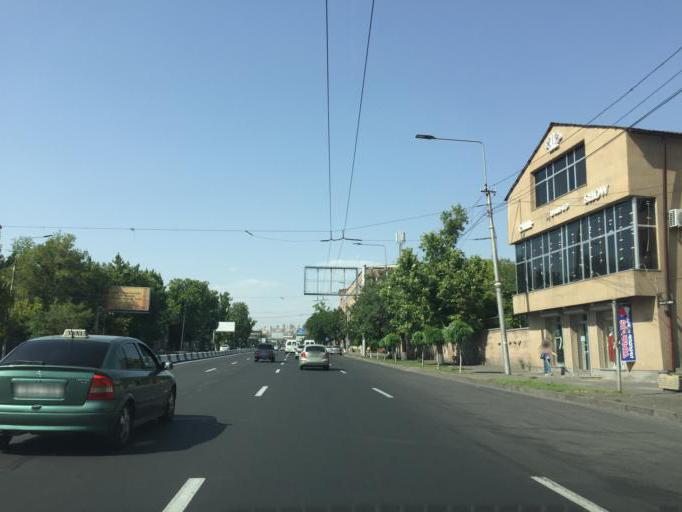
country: AM
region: Yerevan
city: Yerevan
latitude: 40.1590
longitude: 44.5029
